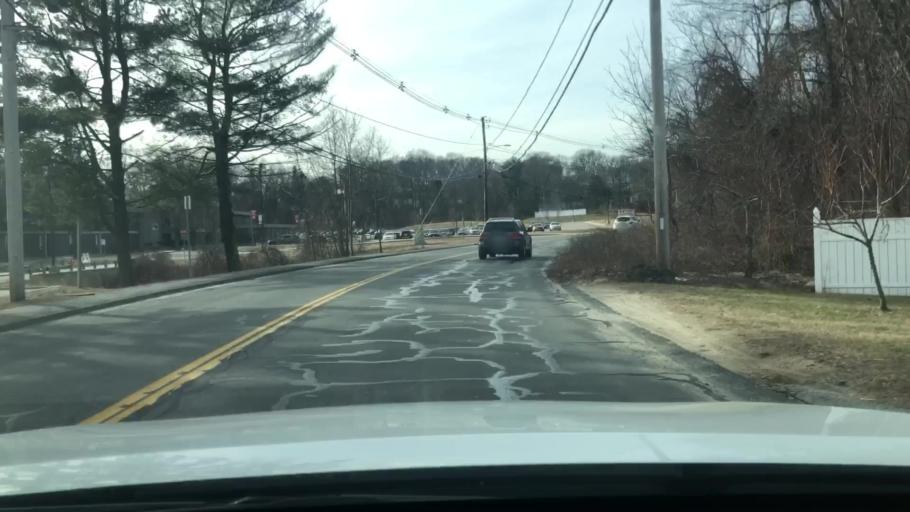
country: US
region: Massachusetts
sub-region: Worcester County
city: Milford
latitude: 42.1505
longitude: -71.5339
